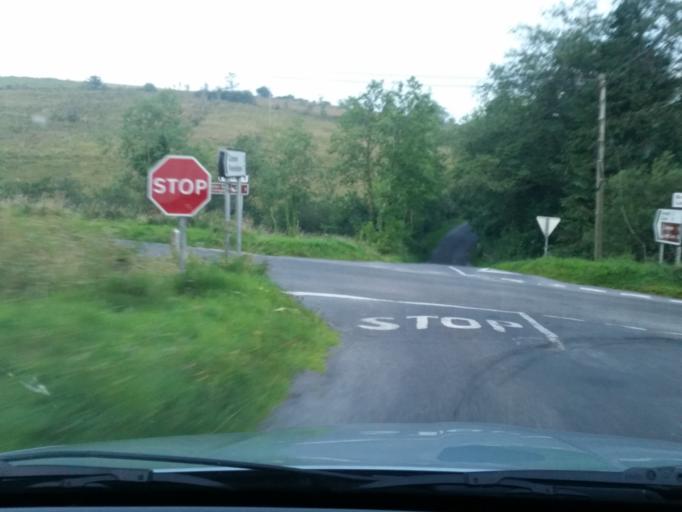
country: GB
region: Northern Ireland
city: Fivemiletown
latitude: 54.2913
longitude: -7.2799
